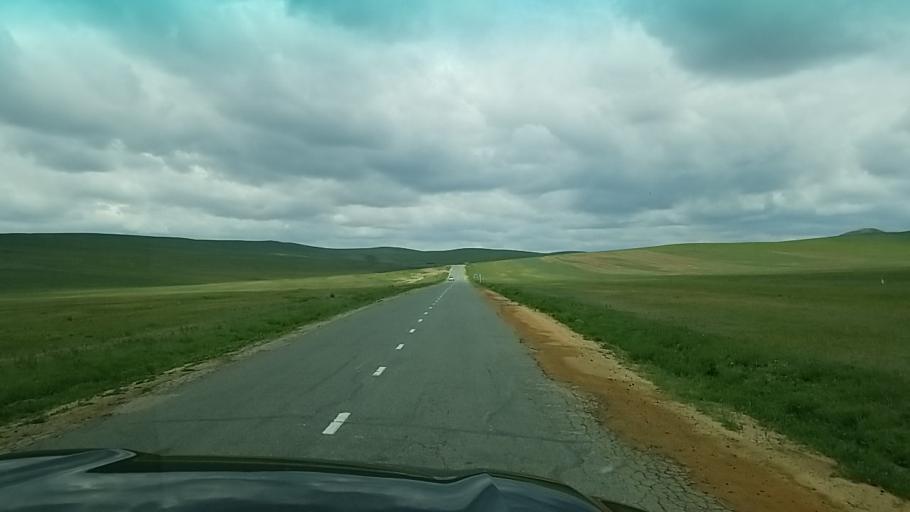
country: MN
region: Darhan Uul
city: Hongor
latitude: 49.1090
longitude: 106.0371
